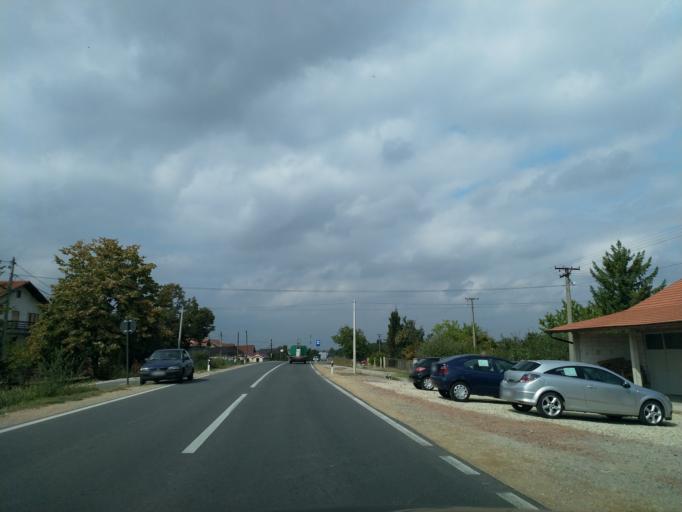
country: RS
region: Central Serbia
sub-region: Sumadijski Okrug
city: Kragujevac
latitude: 44.0794
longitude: 20.8710
